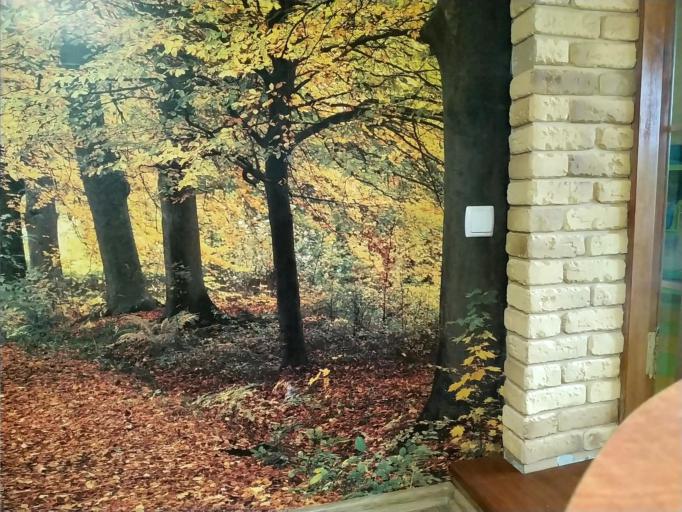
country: BY
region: Mogilev
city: Khotsimsk
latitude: 53.5467
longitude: 32.5108
